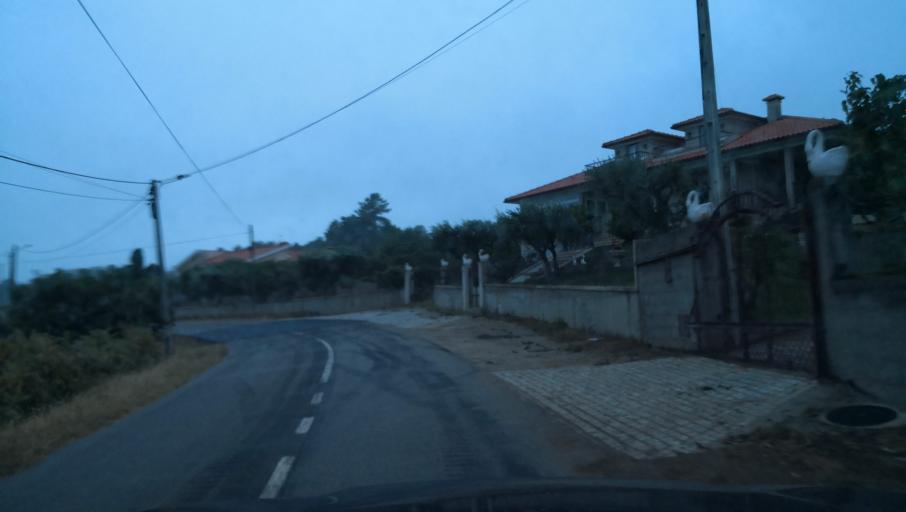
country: PT
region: Vila Real
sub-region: Sabrosa
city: Sabrosa
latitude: 41.2637
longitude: -7.6000
